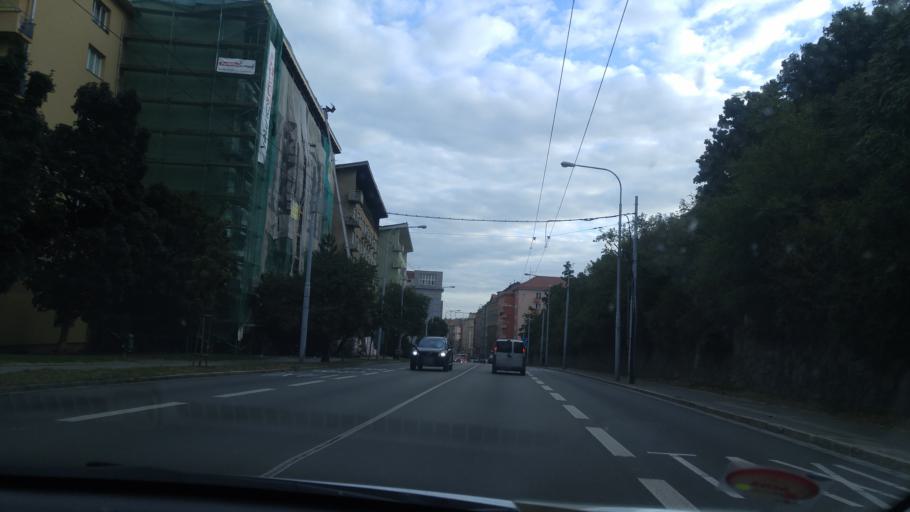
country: CZ
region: South Moravian
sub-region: Mesto Brno
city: Brno
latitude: 49.2019
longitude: 16.5927
